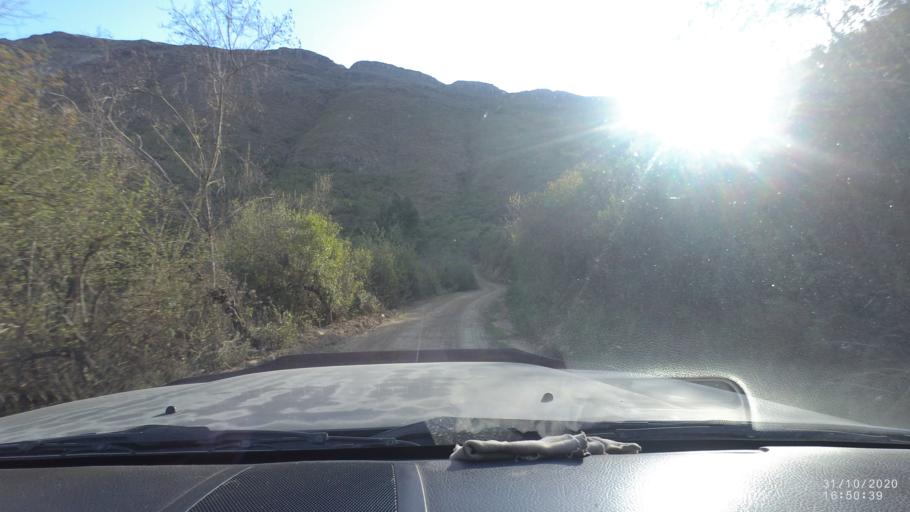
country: BO
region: Chuquisaca
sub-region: Provincia Zudanez
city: Mojocoya
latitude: -18.5095
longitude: -64.5713
